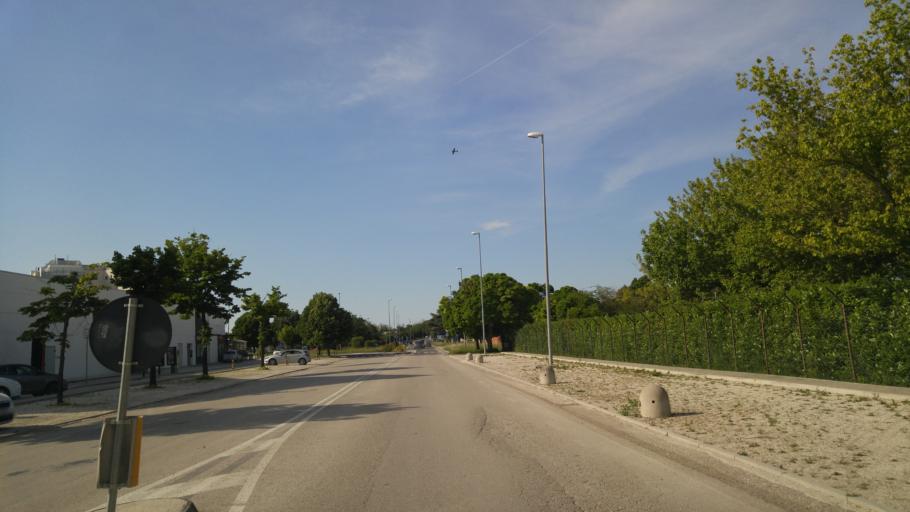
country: IT
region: The Marches
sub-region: Provincia di Pesaro e Urbino
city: Bellocchi
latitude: 43.8007
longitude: 13.0162
